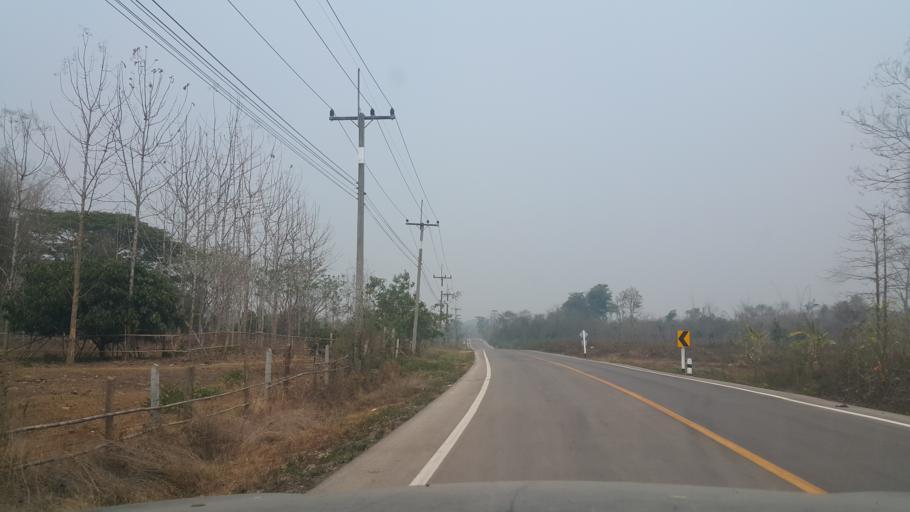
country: TH
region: Lampang
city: Soem Ngam
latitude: 18.2067
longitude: 99.2138
